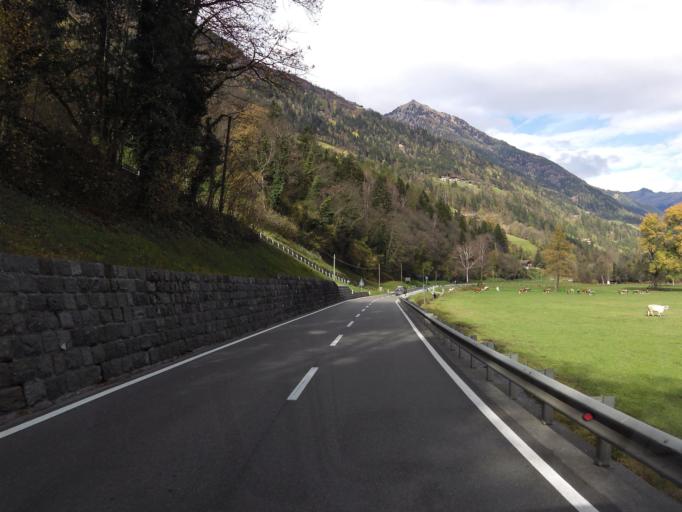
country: IT
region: Trentino-Alto Adige
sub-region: Bolzano
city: San Martino in Passiria
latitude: 46.7496
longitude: 11.2065
